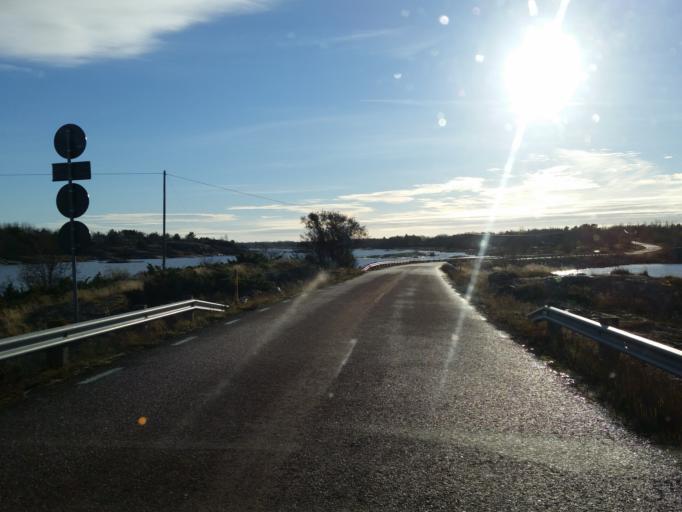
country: AX
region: Alands skaergard
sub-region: Kumlinge
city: Kumlinge
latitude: 60.2565
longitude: 20.7380
